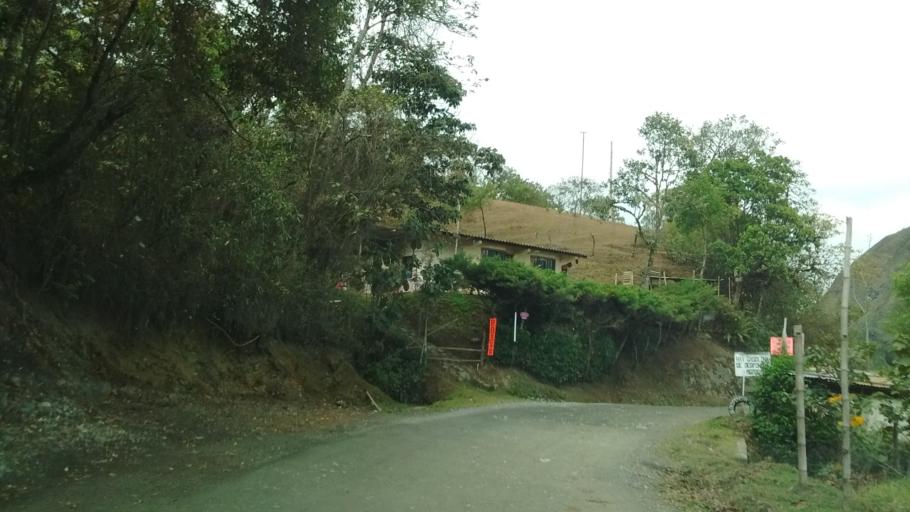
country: CO
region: Cauca
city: Almaguer
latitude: 1.8567
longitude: -76.9415
